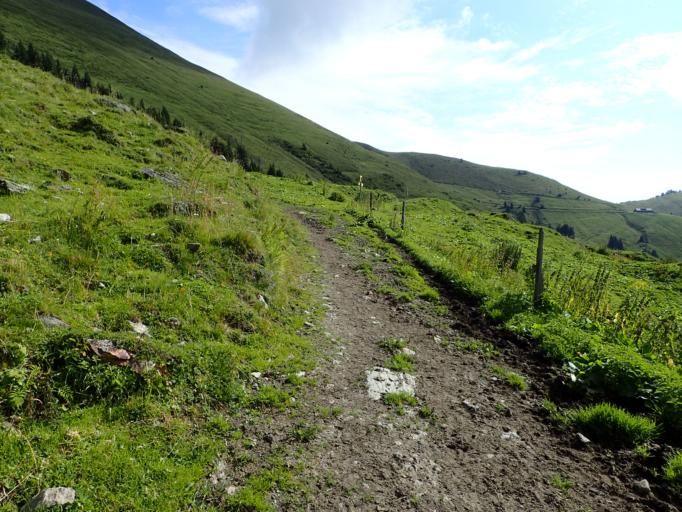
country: AT
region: Salzburg
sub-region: Politischer Bezirk Zell am See
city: Taxenbach
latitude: 47.3438
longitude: 12.9540
